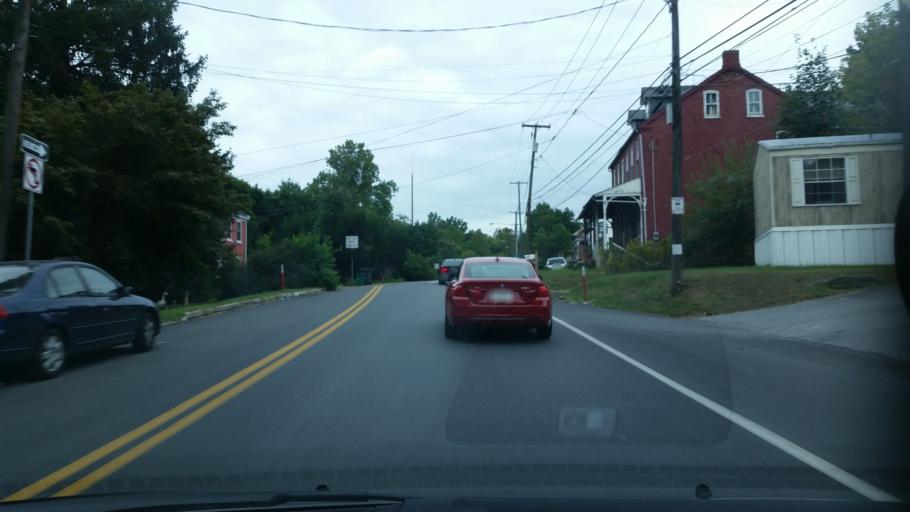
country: US
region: Pennsylvania
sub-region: Lancaster County
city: Lancaster
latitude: 40.0201
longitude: -76.3034
